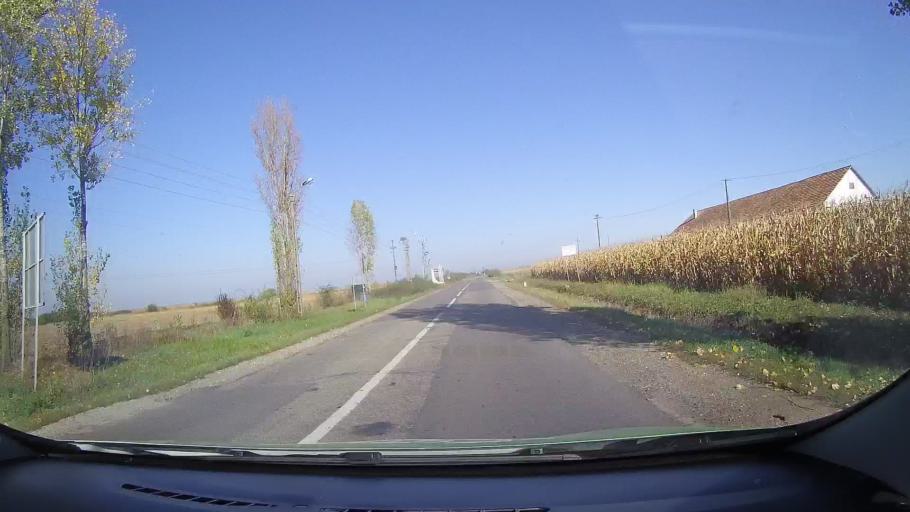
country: RO
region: Satu Mare
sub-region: Oras Tasnad
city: Tasnad
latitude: 47.5158
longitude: 22.5721
